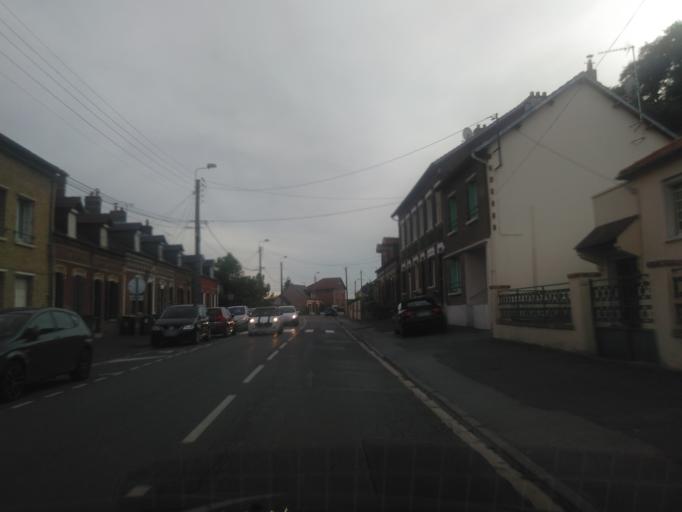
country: FR
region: Picardie
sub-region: Departement de l'Aisne
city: Laon
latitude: 49.5631
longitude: 3.6347
